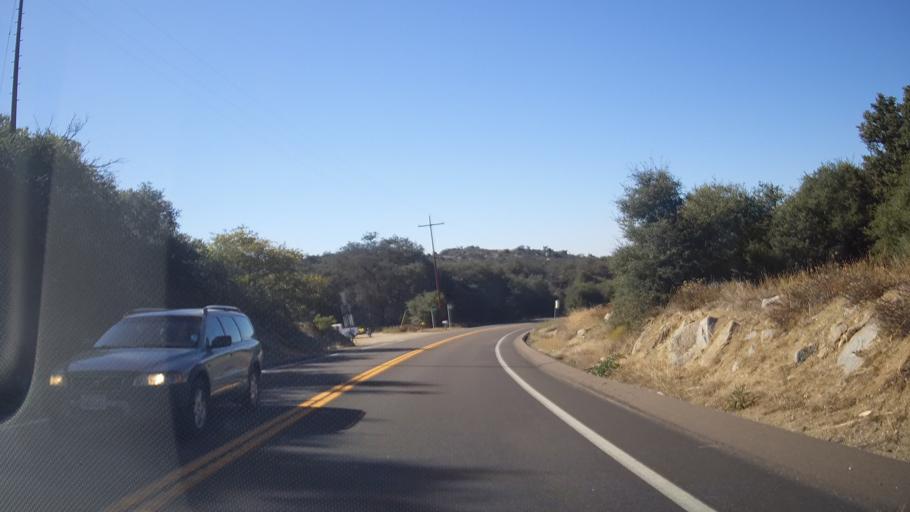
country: US
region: California
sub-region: San Diego County
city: Julian
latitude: 33.0804
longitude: -116.6437
